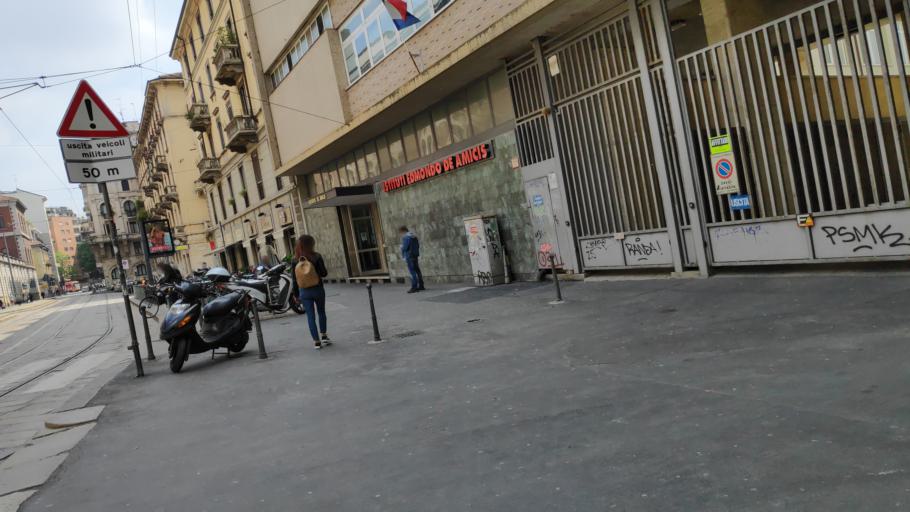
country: IT
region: Lombardy
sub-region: Citta metropolitana di Milano
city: Milano
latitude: 45.4570
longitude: 9.2010
